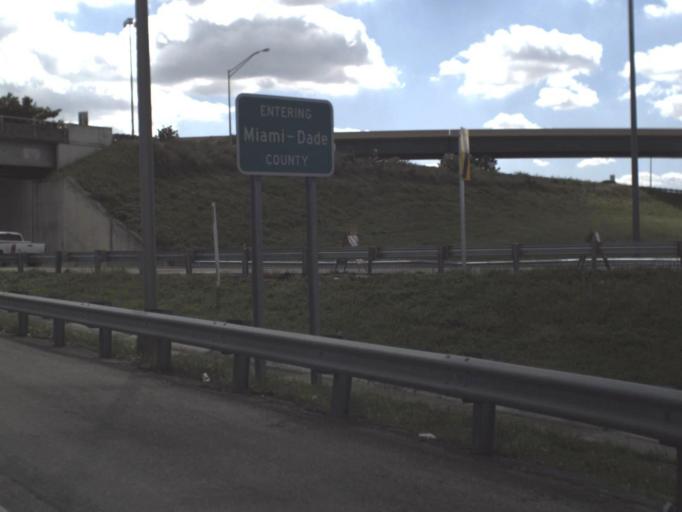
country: US
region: Florida
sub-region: Broward County
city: Miramar
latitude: 25.9738
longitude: -80.2299
